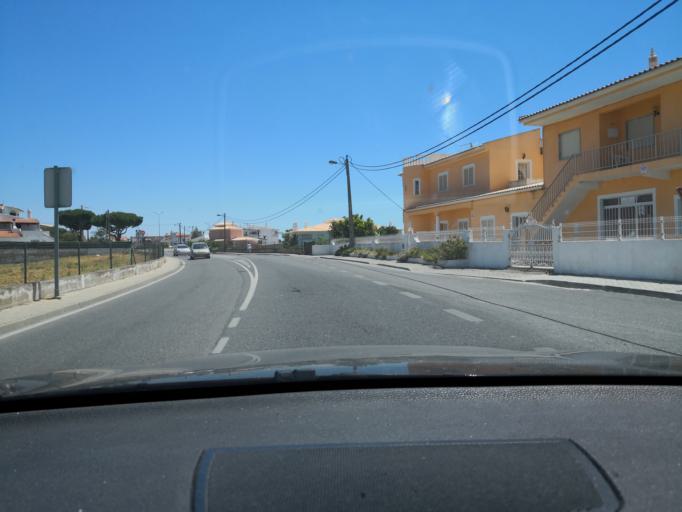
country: PT
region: Faro
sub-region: Albufeira
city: Ferreiras
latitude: 37.1043
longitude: -8.1967
